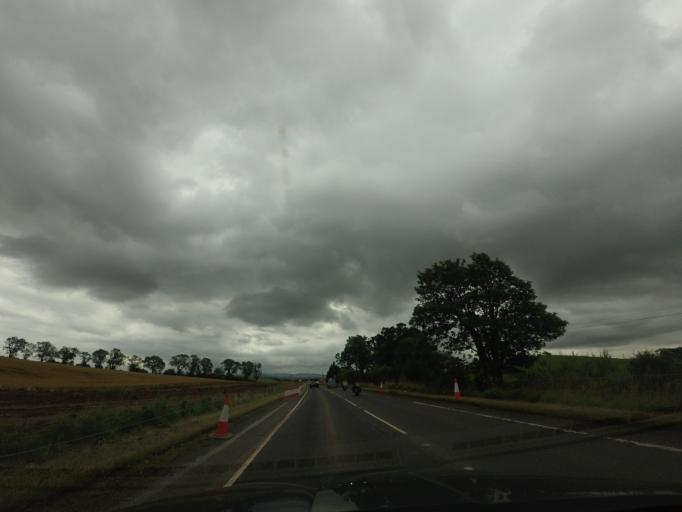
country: GB
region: Scotland
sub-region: Perth and Kinross
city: Bankfoot
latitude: 56.4814
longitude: -3.4954
